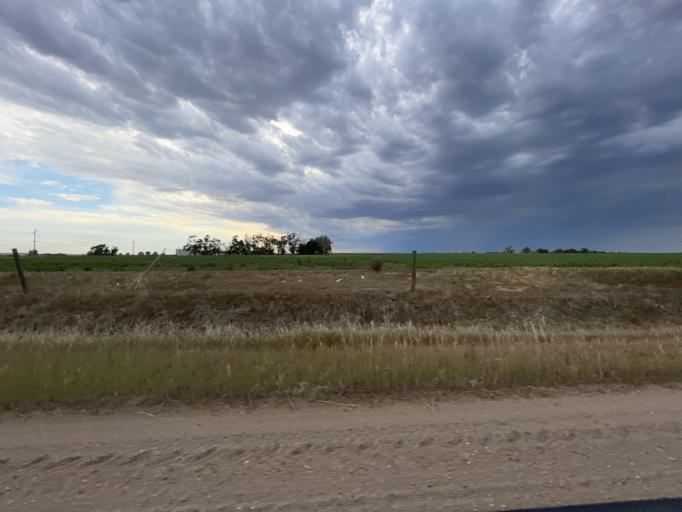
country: US
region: Nebraska
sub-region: Red Willow County
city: McCook
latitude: 40.2511
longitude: -100.7601
